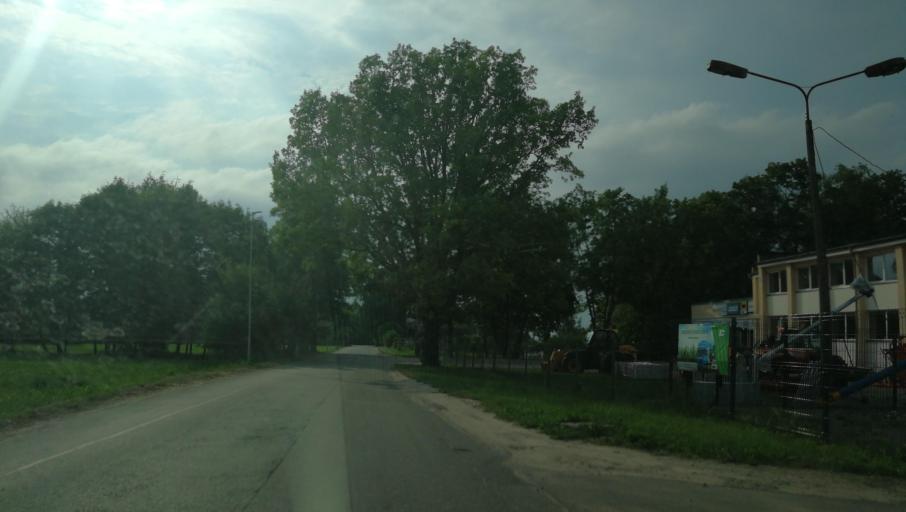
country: LV
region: Cesu Rajons
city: Cesis
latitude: 57.3206
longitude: 25.2958
